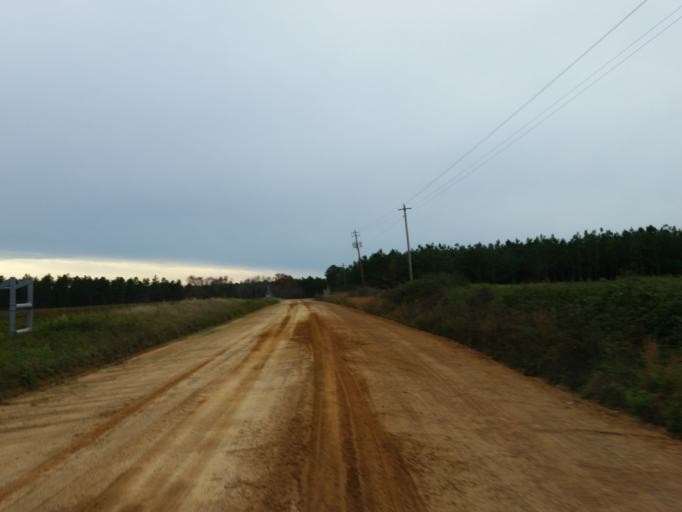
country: US
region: Georgia
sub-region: Crisp County
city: Cordele
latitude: 31.8834
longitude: -83.7202
